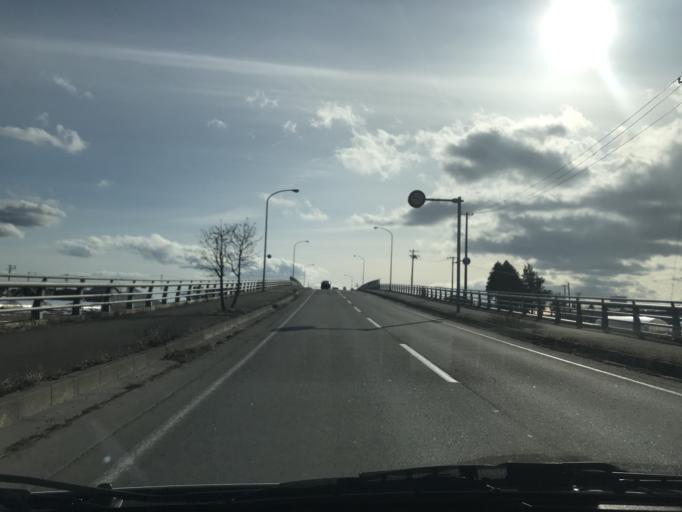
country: JP
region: Iwate
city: Kitakami
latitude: 39.2972
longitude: 141.0981
